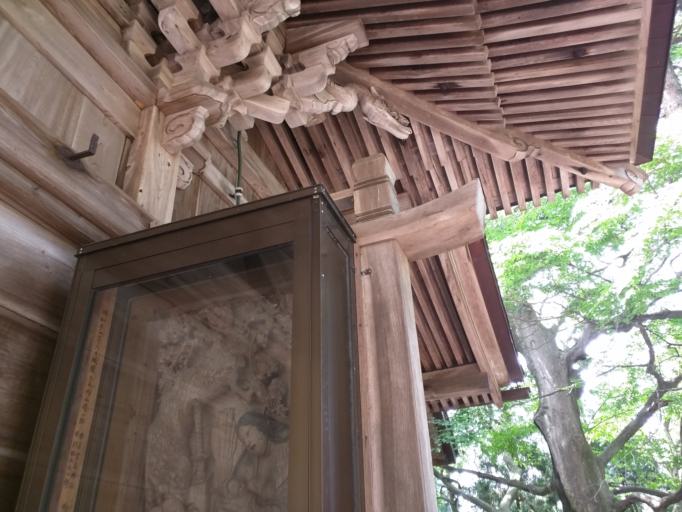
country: JP
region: Niigata
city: Sanjo
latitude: 37.5766
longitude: 138.9566
